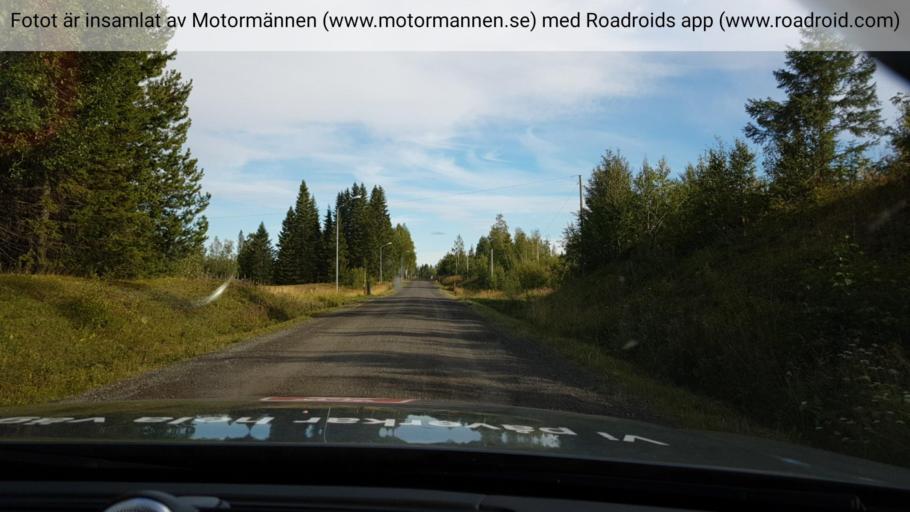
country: SE
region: Jaemtland
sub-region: Stroemsunds Kommun
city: Stroemsund
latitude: 64.1266
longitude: 15.7983
